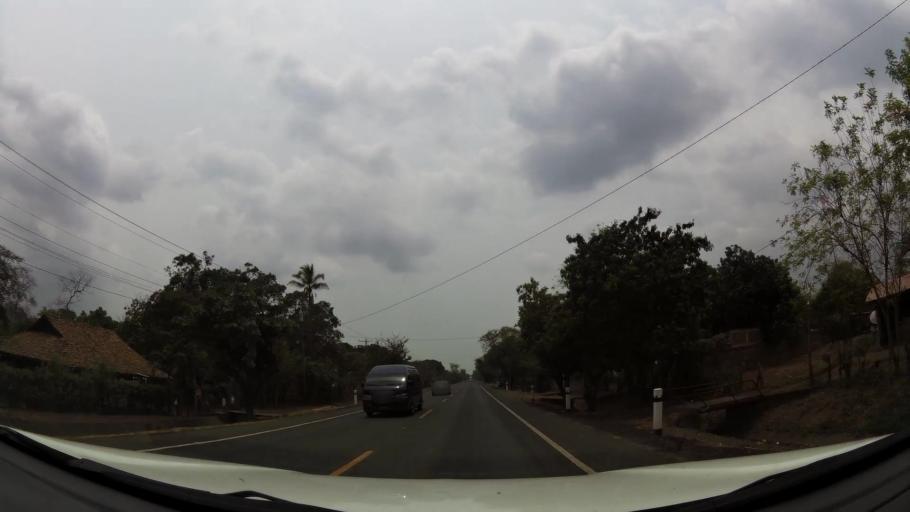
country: NI
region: Leon
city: Telica
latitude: 12.5252
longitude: -86.8769
